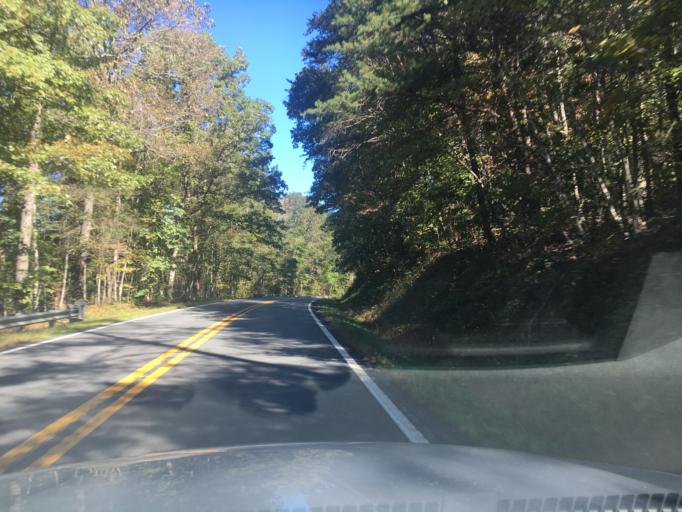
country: US
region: North Carolina
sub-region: Rutherford County
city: Spindale
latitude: 35.4732
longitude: -81.8833
